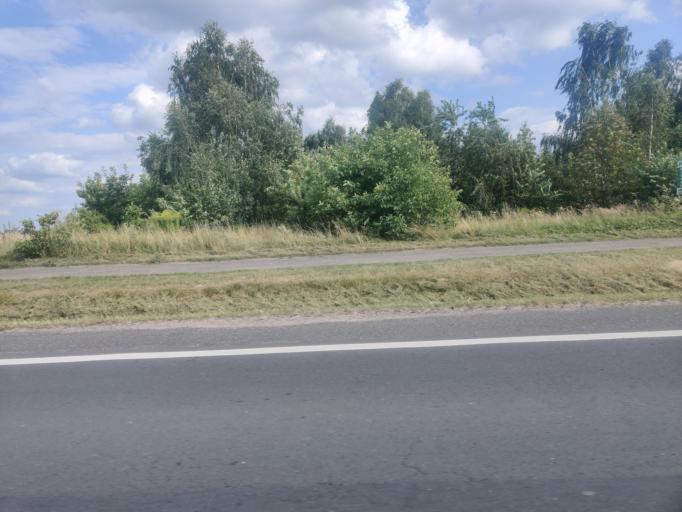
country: PL
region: Greater Poland Voivodeship
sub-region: Konin
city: Konin
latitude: 52.1982
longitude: 18.2689
